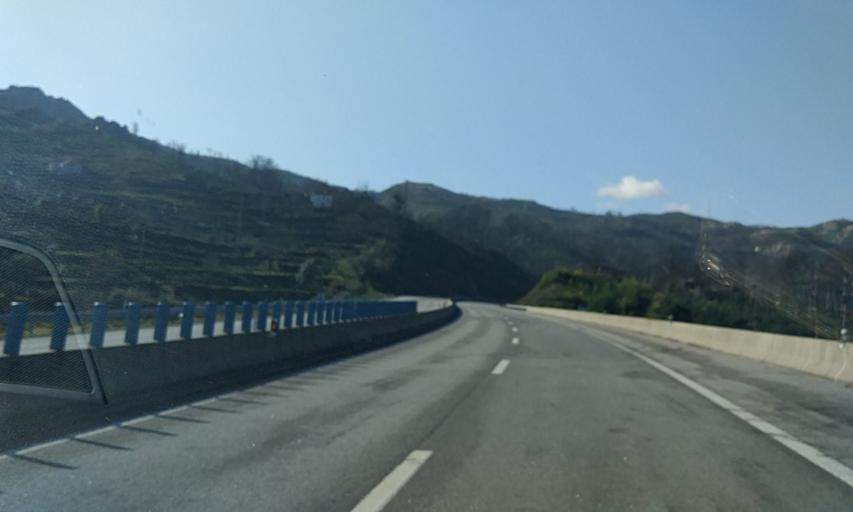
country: PT
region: Viseu
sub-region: Vouzela
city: Vouzela
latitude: 40.6953
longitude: -8.0919
